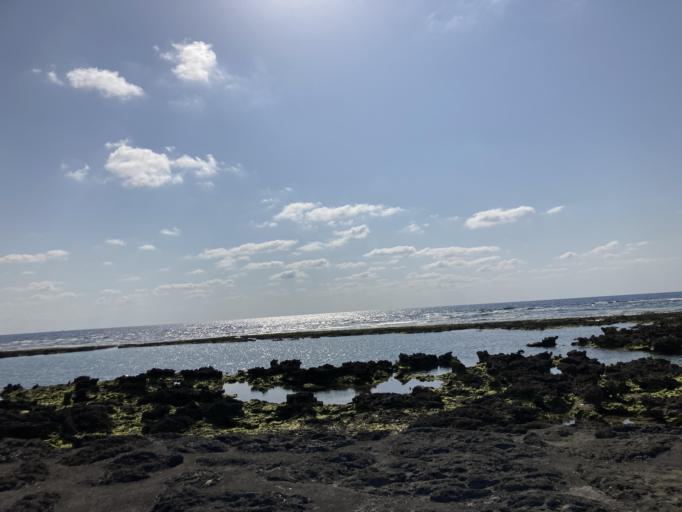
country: JP
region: Okinawa
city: Itoman
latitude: 26.1148
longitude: 127.7447
